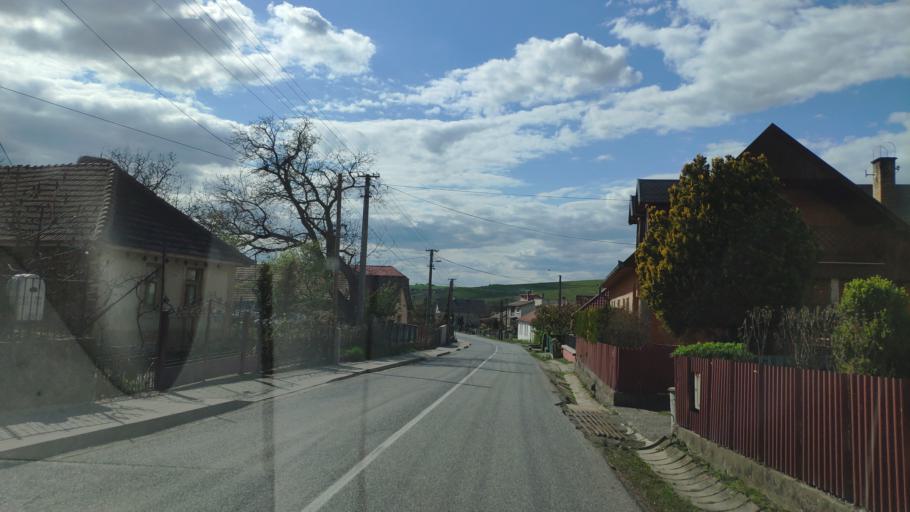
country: SK
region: Kosicky
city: Kosice
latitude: 48.6583
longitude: 21.4031
